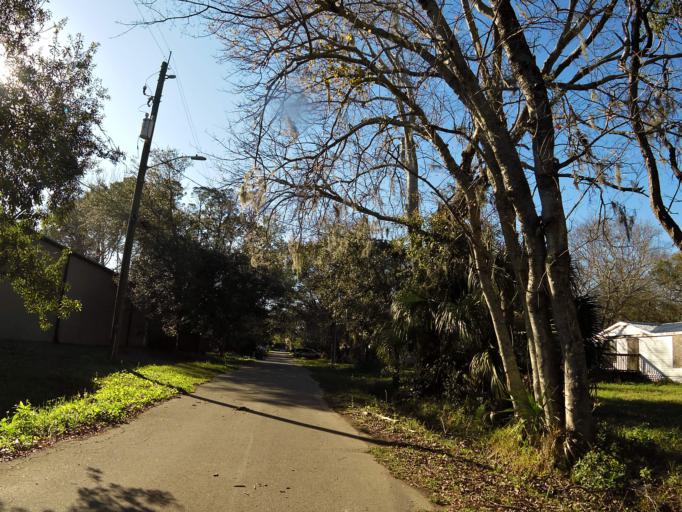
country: US
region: Florida
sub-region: Duval County
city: Jacksonville
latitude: 30.2724
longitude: -81.6283
